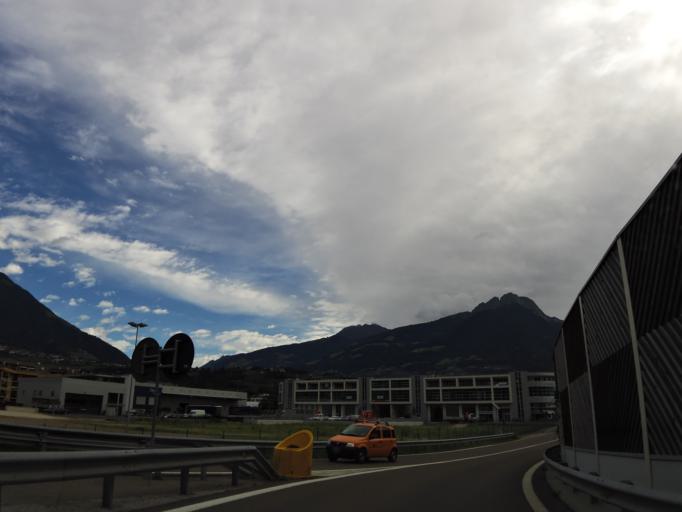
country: IT
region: Trentino-Alto Adige
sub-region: Bolzano
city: Marlengo
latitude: 46.6609
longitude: 11.1451
